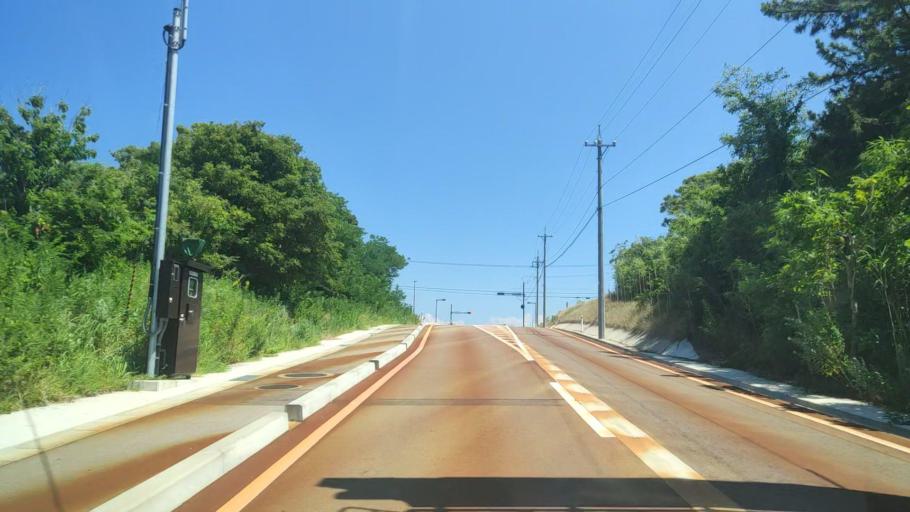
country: JP
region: Ishikawa
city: Kanazawa-shi
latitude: 36.6733
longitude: 136.6546
